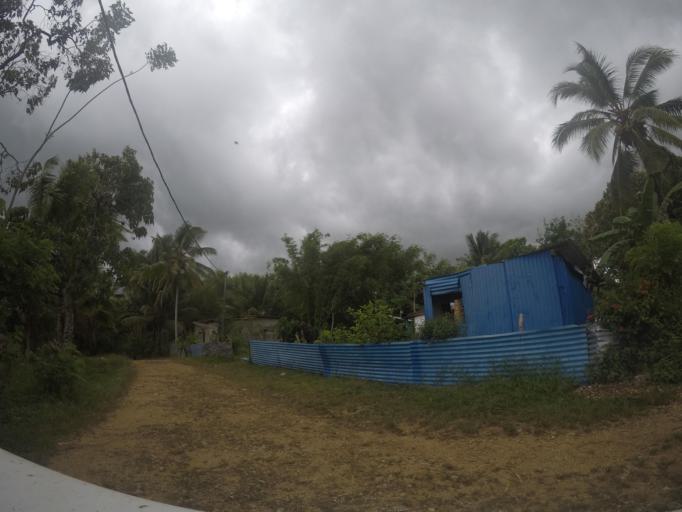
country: TL
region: Lautem
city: Lospalos
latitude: -8.5235
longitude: 126.9881
